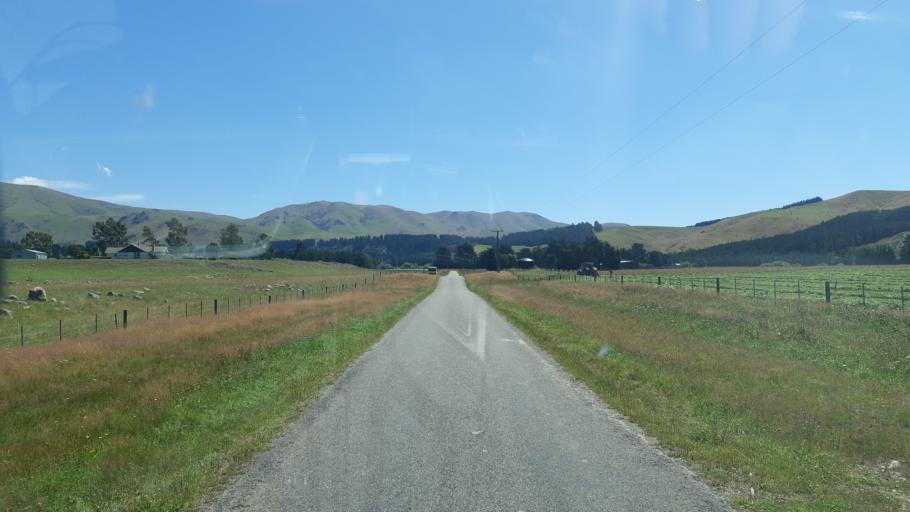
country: NZ
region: Canterbury
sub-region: Timaru District
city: Pleasant Point
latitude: -44.3343
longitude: 170.8883
